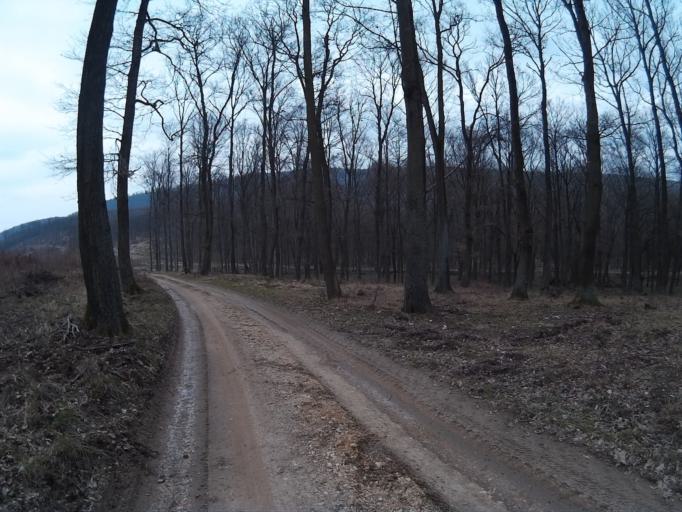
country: HU
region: Veszprem
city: Zirc
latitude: 47.1868
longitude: 17.8989
